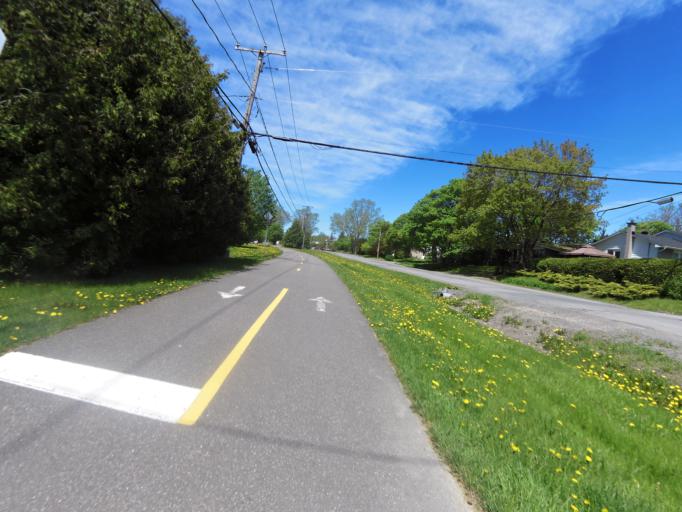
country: CA
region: Ontario
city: Bells Corners
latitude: 45.4026
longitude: -75.8677
